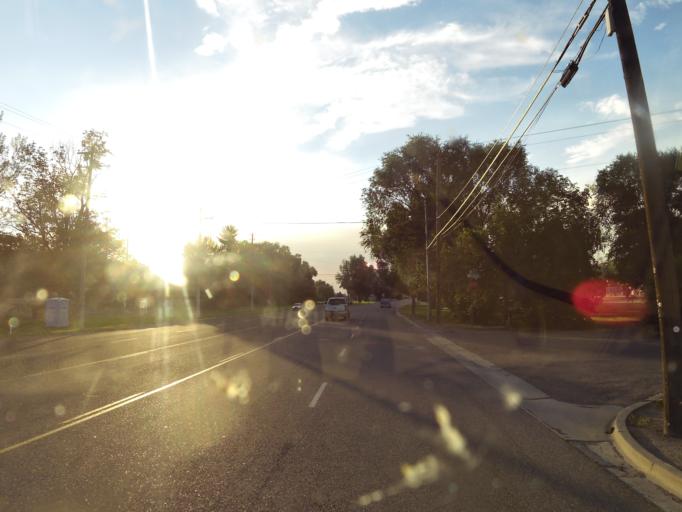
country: US
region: Idaho
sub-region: Bannock County
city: Pocatello
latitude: 42.8446
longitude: -112.4180
